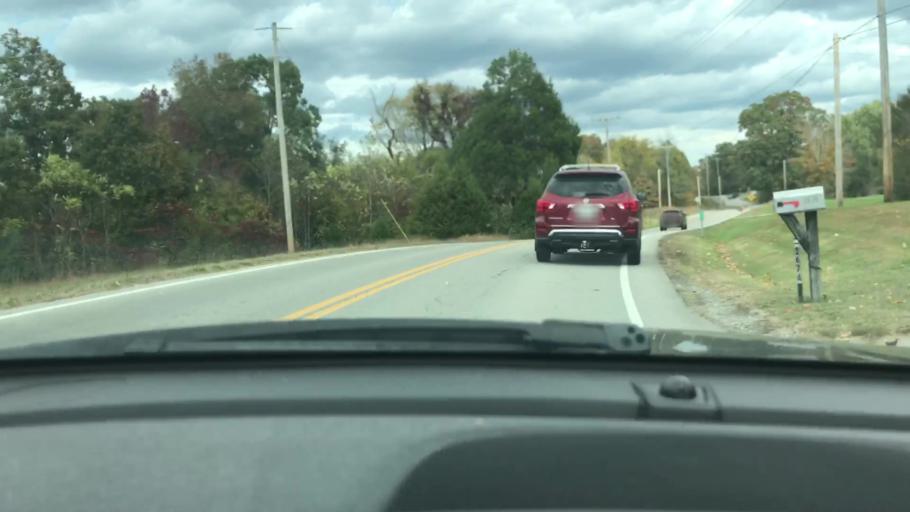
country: US
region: Tennessee
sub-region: Dickson County
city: Charlotte
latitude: 36.2453
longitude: -87.2419
